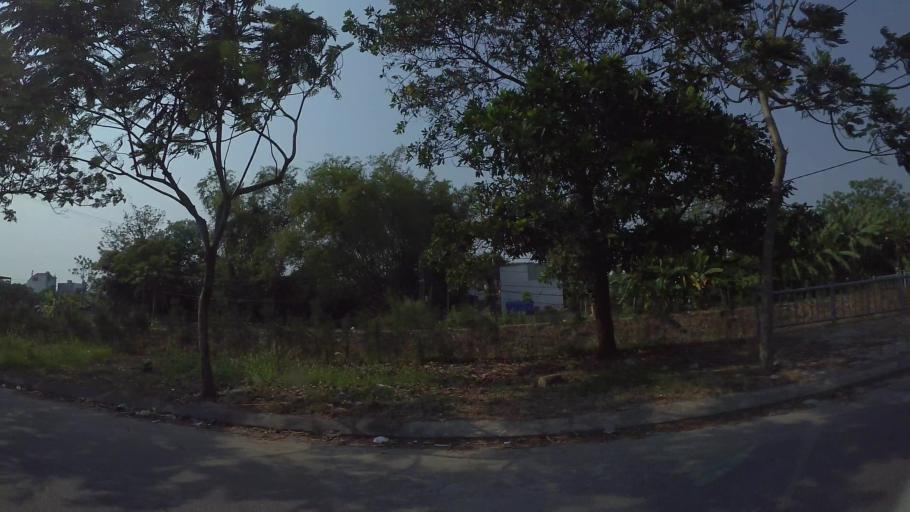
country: VN
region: Da Nang
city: Cam Le
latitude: 16.0093
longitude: 108.1994
